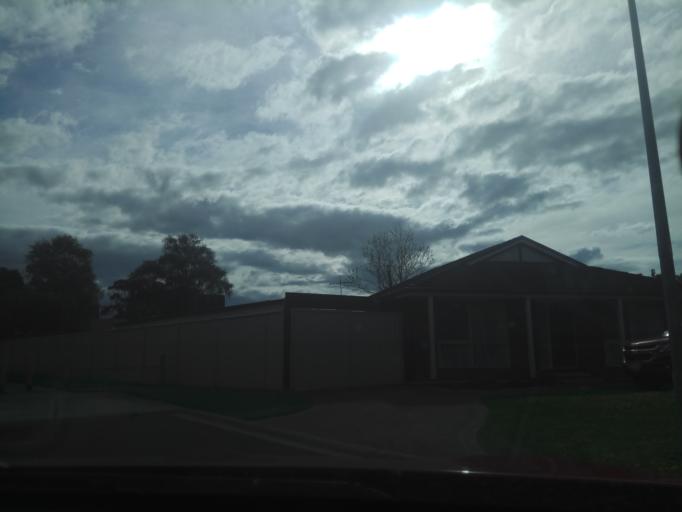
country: AU
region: Victoria
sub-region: Casey
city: Cranbourne North
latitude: -38.0721
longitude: 145.2731
